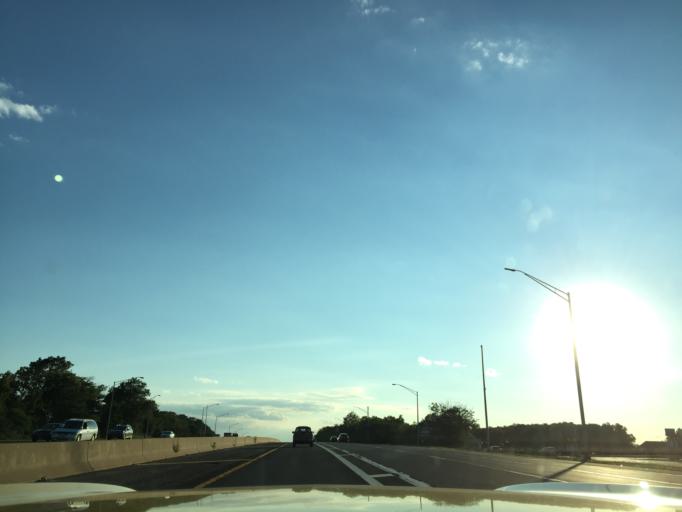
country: US
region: New York
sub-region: Suffolk County
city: Hauppauge
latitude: 40.8087
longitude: -73.2207
